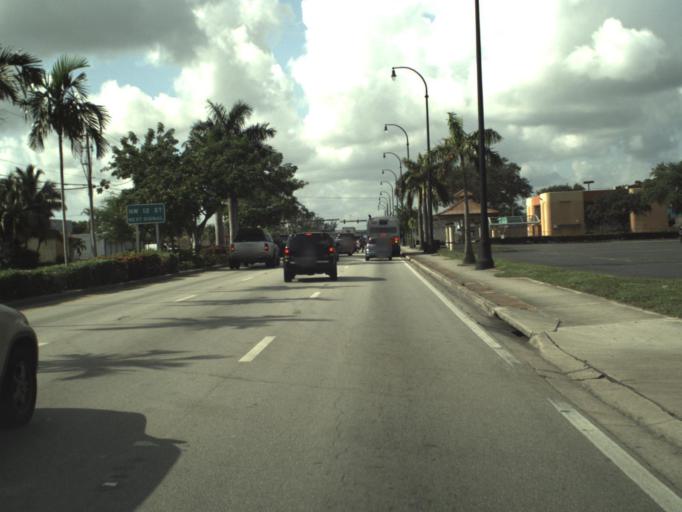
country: US
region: Florida
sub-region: Broward County
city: Lauderhill
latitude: 26.1432
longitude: -80.2028
